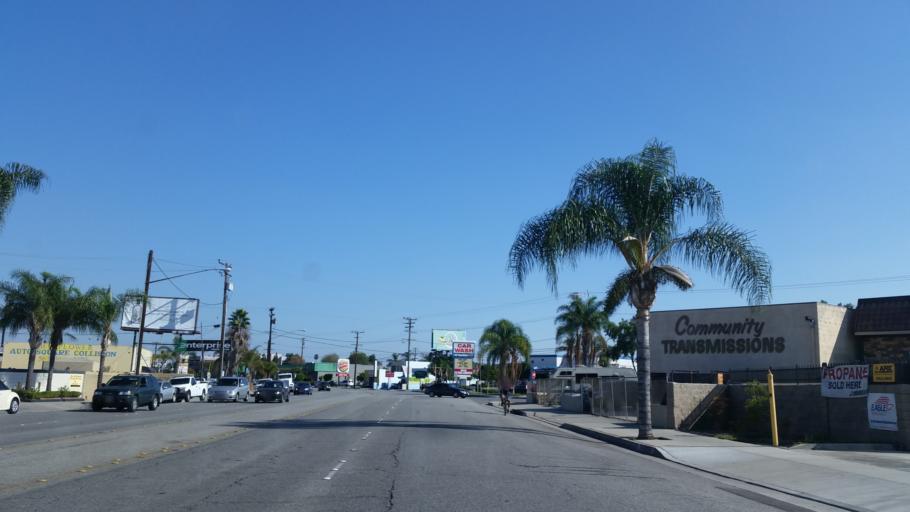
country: US
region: California
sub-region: Los Angeles County
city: Bellflower
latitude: 33.8737
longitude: -118.1202
